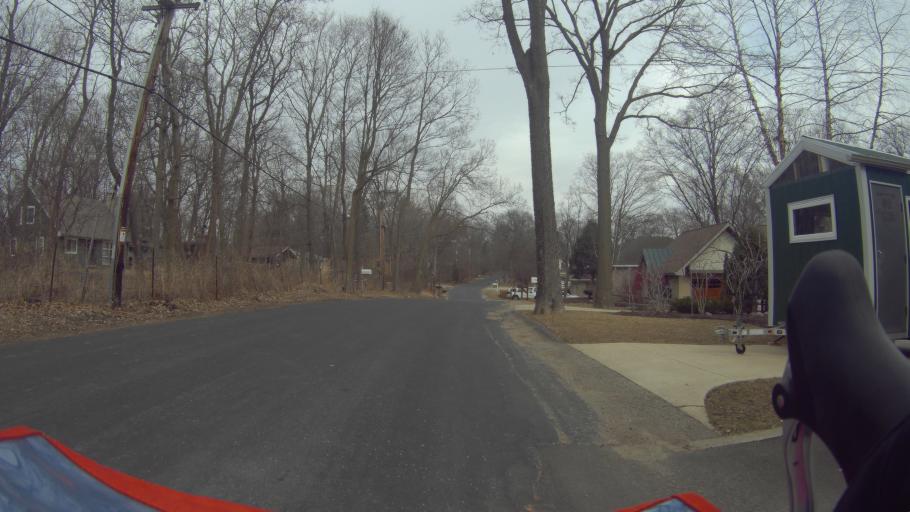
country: US
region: Wisconsin
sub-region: Dane County
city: Maple Bluff
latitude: 43.1304
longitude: -89.3864
